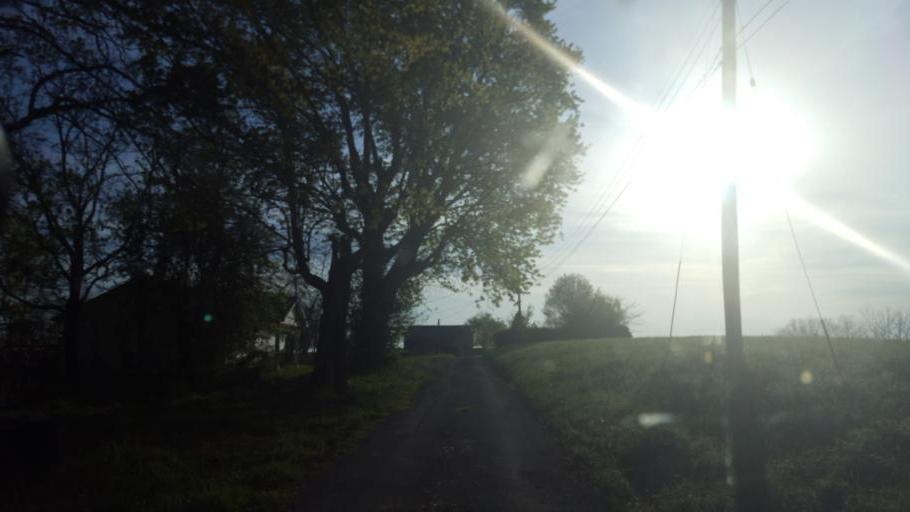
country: US
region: Kentucky
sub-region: Hart County
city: Munfordville
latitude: 37.2636
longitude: -85.8874
